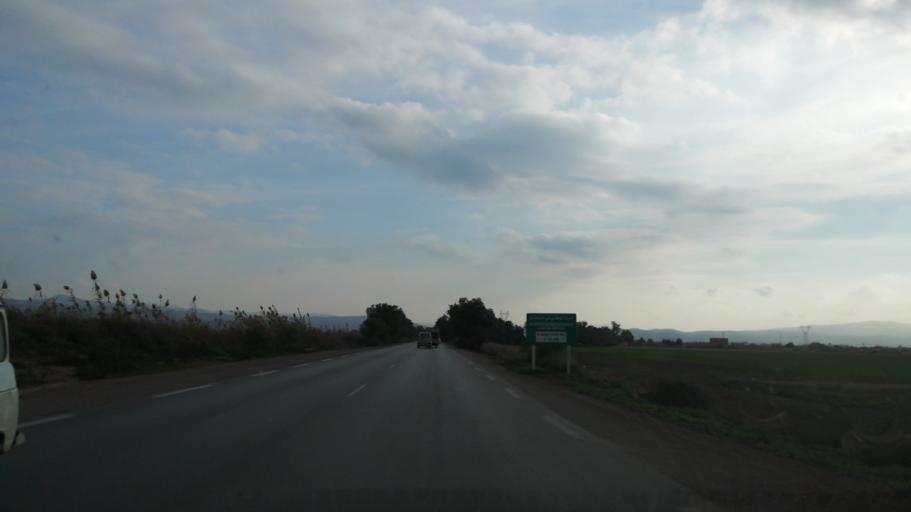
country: DZ
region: Mascara
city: Mascara
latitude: 35.6415
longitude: 0.0603
